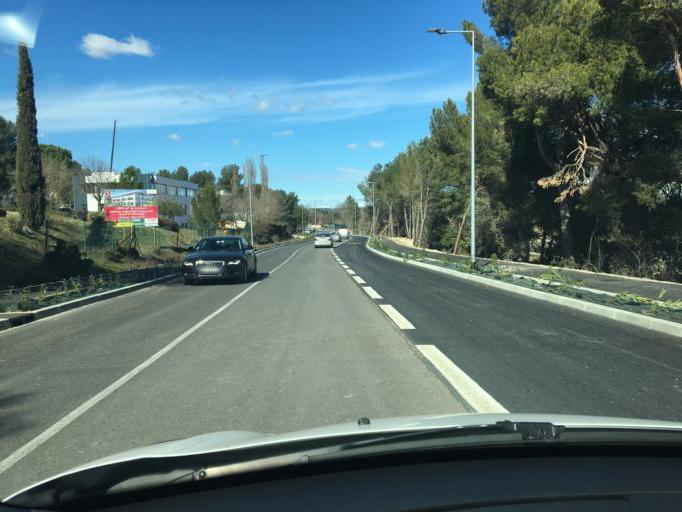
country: FR
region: Provence-Alpes-Cote d'Azur
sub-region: Departement des Bouches-du-Rhone
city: Cabries
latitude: 43.4826
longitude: 5.3648
